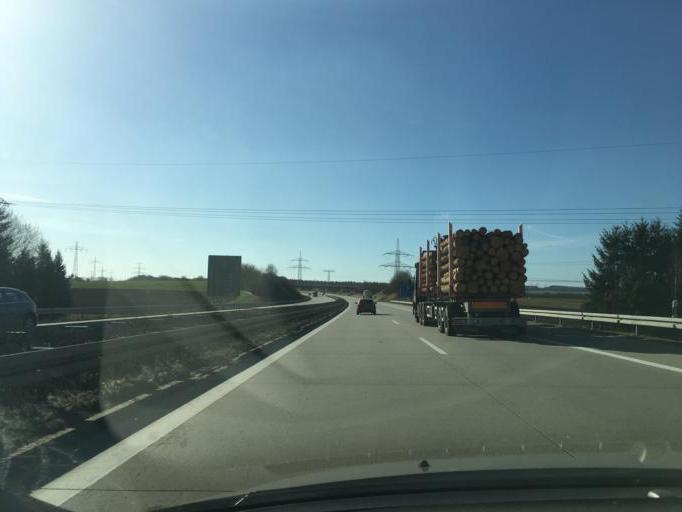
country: DE
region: Saxony
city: Hartmannsdorf
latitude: 50.8759
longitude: 12.7865
